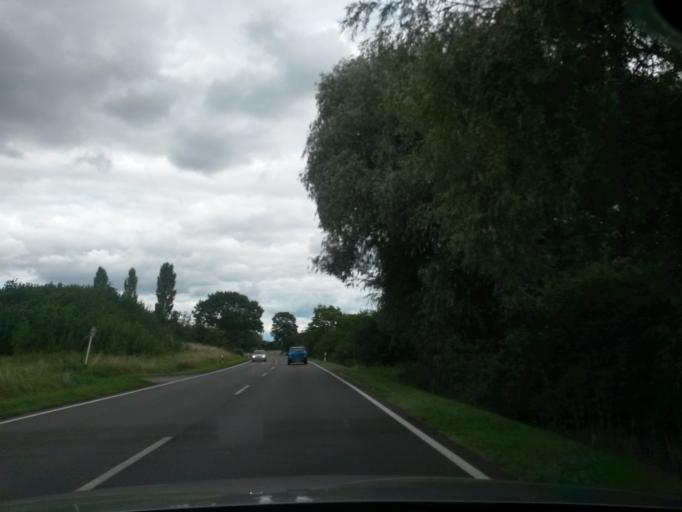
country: DE
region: Brandenburg
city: Angermunde
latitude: 53.0109
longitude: 14.0074
